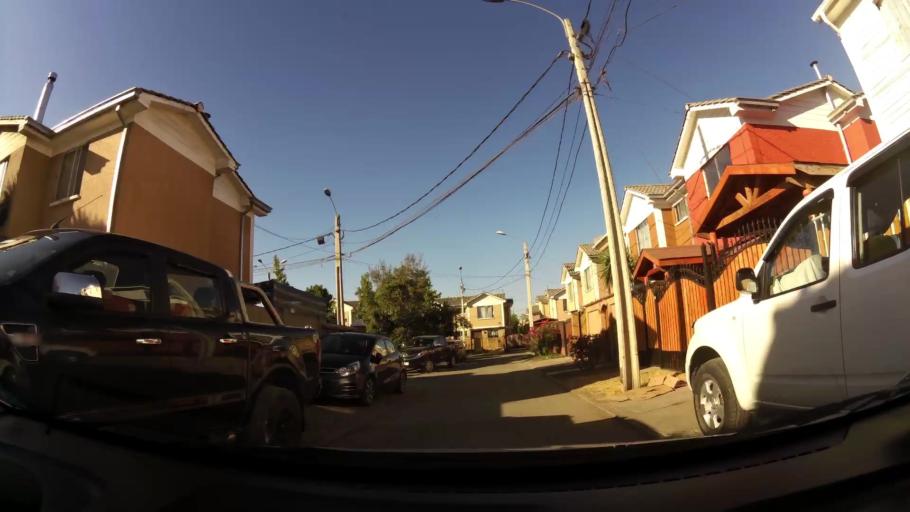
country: CL
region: O'Higgins
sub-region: Provincia de Cachapoal
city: Rancagua
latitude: -34.1852
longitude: -70.7621
